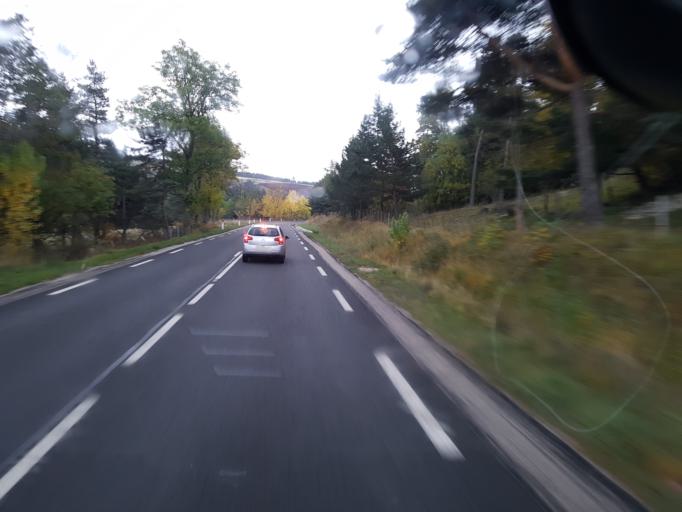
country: FR
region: Languedoc-Roussillon
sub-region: Departement de la Lozere
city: Mende
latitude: 44.5573
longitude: 3.6227
